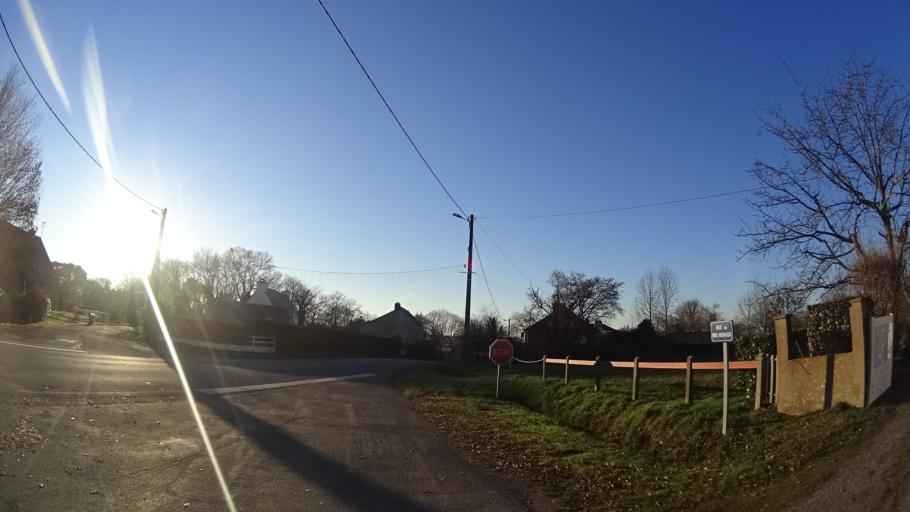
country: FR
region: Brittany
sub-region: Departement du Morbihan
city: Saint-Jean-la-Poterie
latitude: 47.6352
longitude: -2.1170
